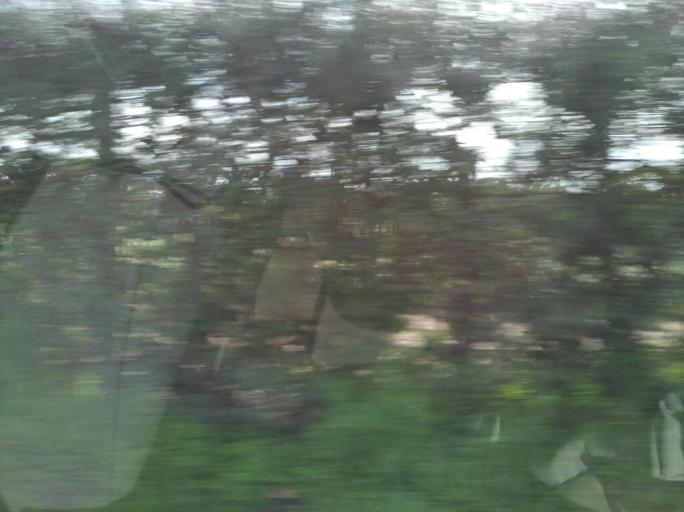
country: CL
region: Valparaiso
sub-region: Provincia de Marga Marga
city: Limache
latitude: -33.0122
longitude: -71.2112
